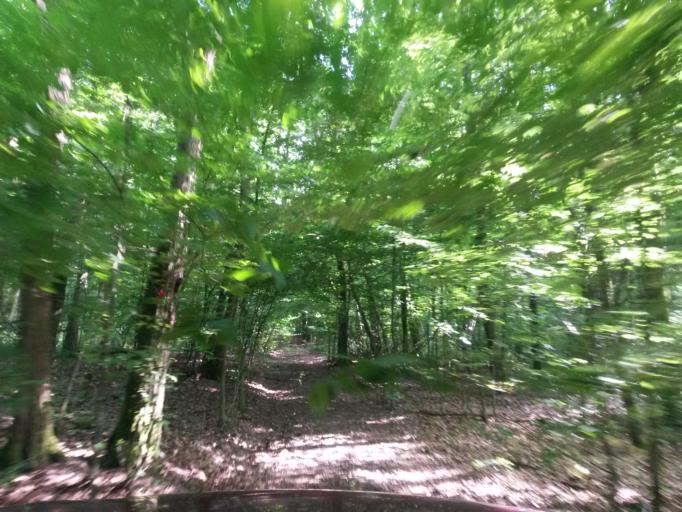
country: SK
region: Kosicky
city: Moldava nad Bodvou
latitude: 48.6171
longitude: 21.1069
